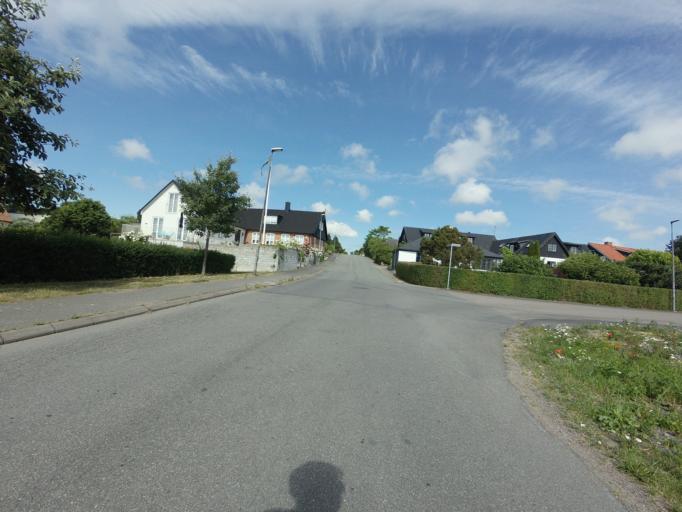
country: SE
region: Skane
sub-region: Simrishamns Kommun
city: Simrishamn
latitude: 55.4763
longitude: 14.2849
